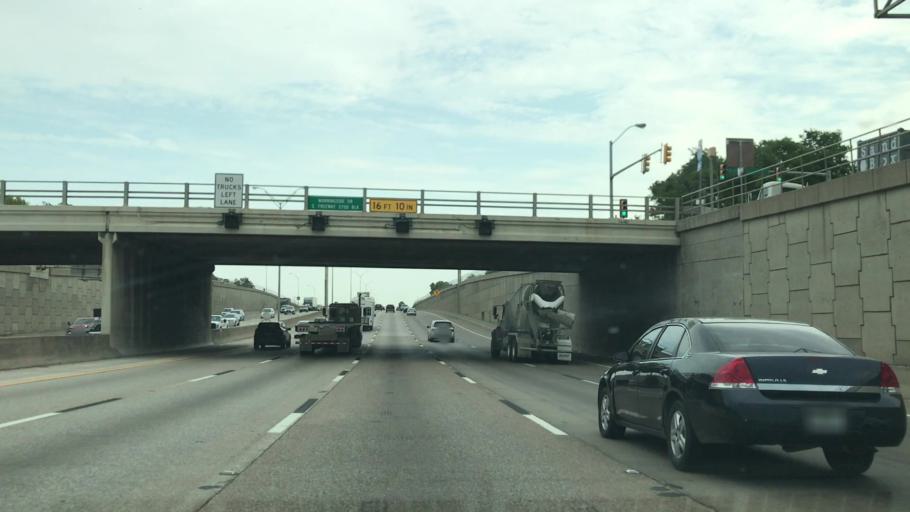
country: US
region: Texas
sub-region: Tarrant County
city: Fort Worth
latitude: 32.7126
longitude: -97.3205
